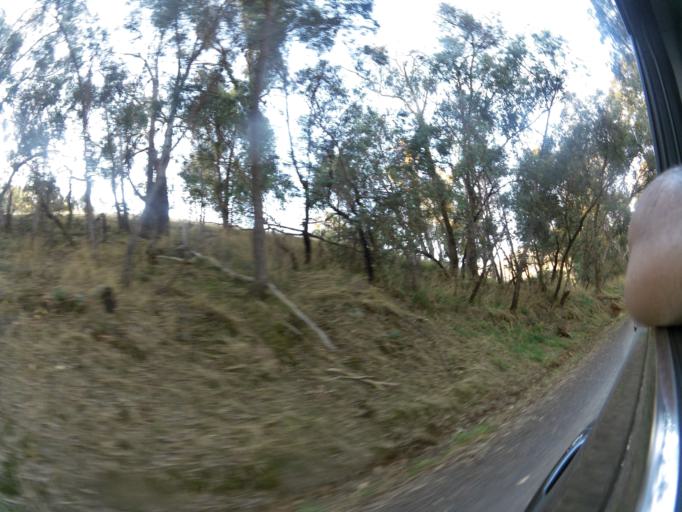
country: AU
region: Victoria
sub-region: Murrindindi
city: Alexandra
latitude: -37.1480
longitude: 145.5245
